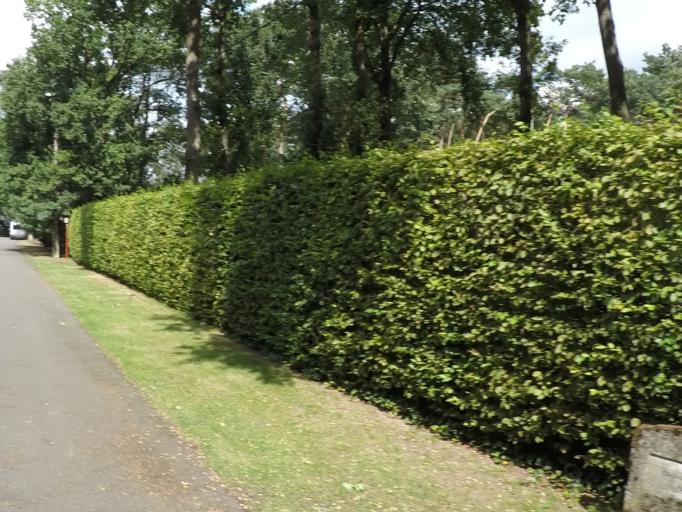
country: BE
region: Flanders
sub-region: Provincie Antwerpen
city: Zandhoven
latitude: 51.1966
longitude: 4.6873
